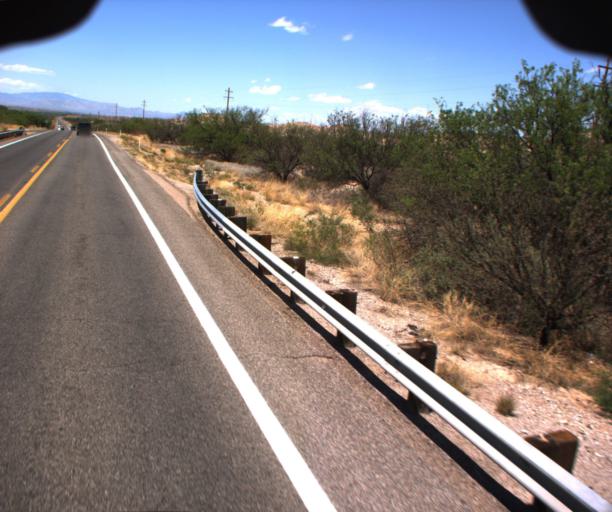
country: US
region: Arizona
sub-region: Cochise County
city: Saint David
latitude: 31.8370
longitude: -110.1864
